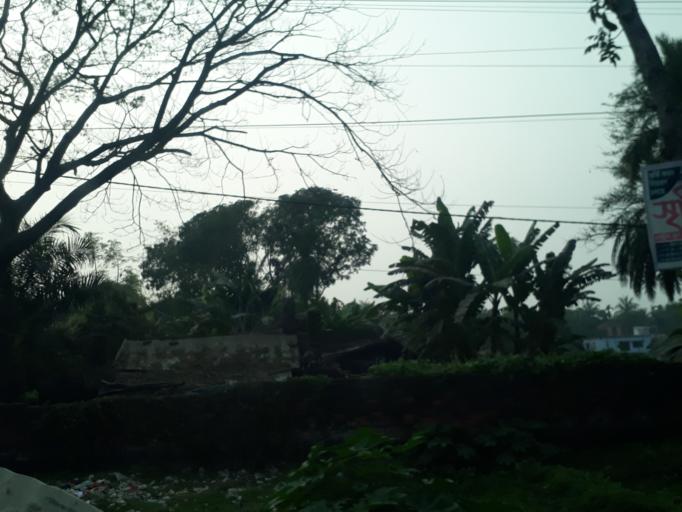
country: BD
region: Khulna
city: Khulna
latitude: 22.9064
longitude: 89.5078
